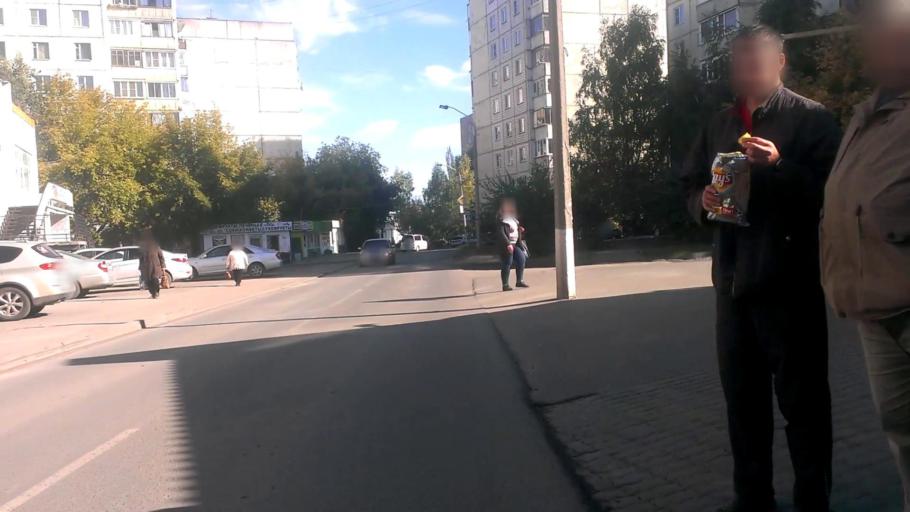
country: RU
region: Altai Krai
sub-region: Gorod Barnaulskiy
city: Barnaul
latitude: 53.3738
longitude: 83.6898
